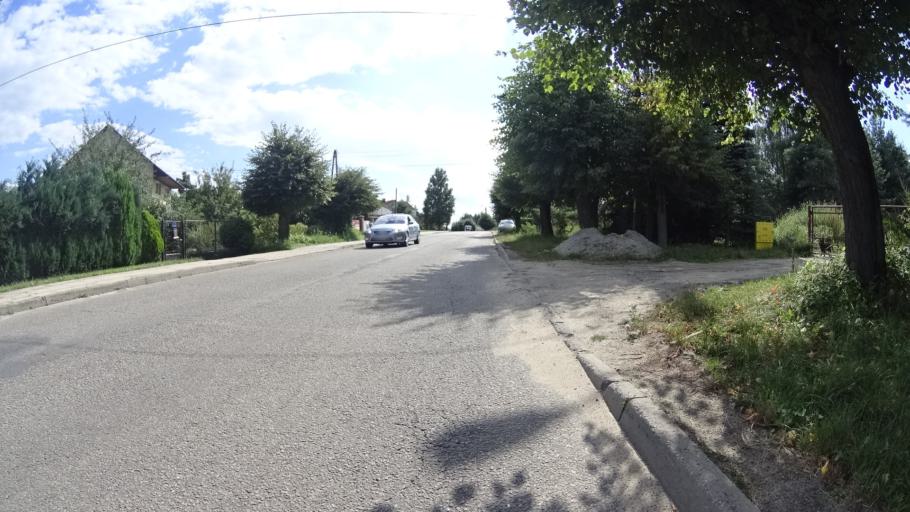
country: PL
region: Masovian Voivodeship
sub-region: Powiat grojecki
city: Mogielnica
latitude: 51.6866
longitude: 20.7186
